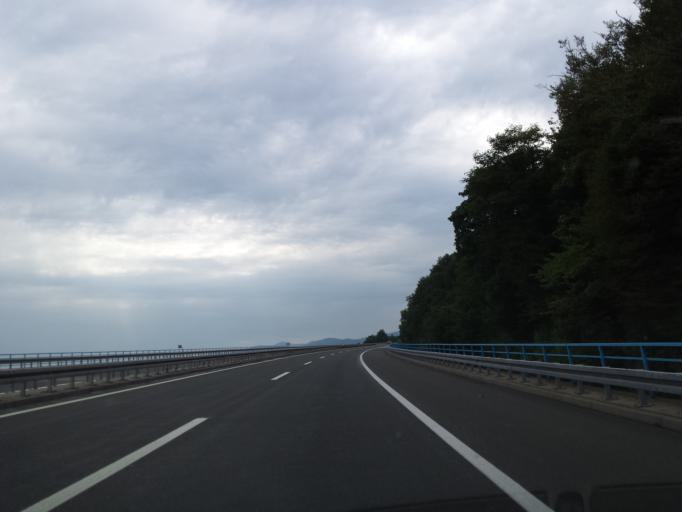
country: HR
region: Karlovacka
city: Ostarije
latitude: 45.1735
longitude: 15.2783
